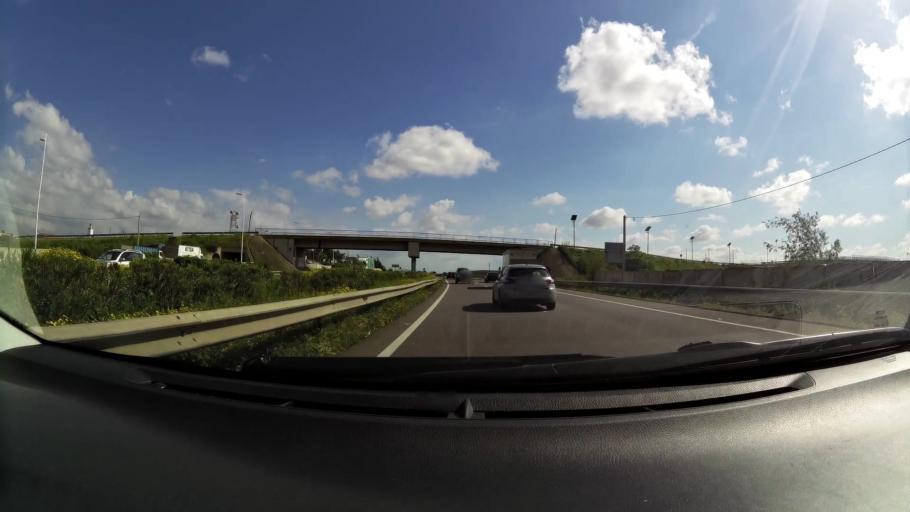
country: MA
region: Chaouia-Ouardigha
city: Nouaseur
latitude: 33.3818
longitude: -7.6216
